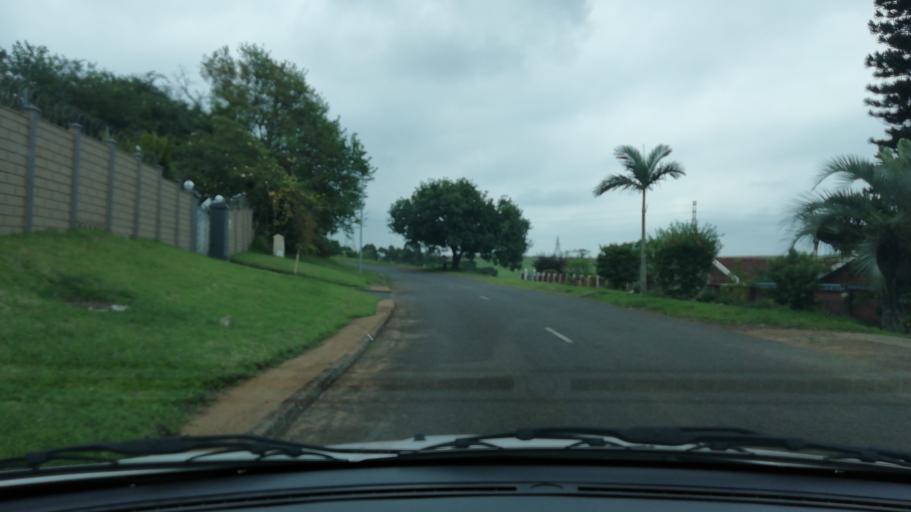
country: ZA
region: KwaZulu-Natal
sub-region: uThungulu District Municipality
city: Empangeni
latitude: -28.7359
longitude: 31.9025
